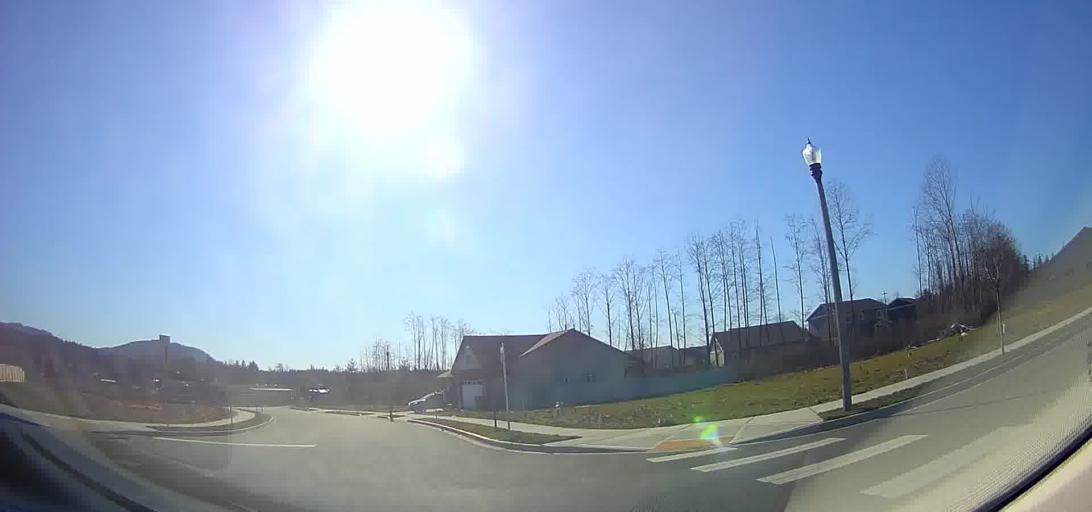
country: US
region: Washington
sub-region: Skagit County
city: Mount Vernon
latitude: 48.4405
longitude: -122.2991
